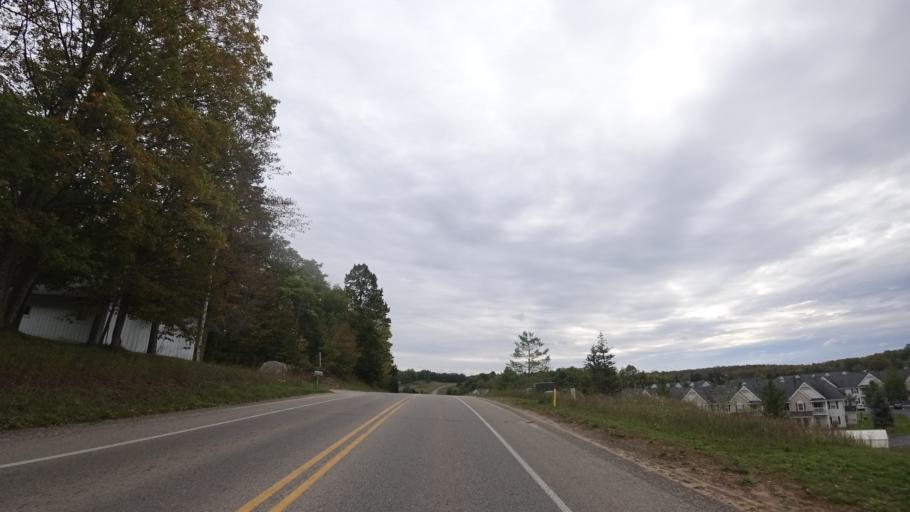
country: US
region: Michigan
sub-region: Emmet County
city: Petoskey
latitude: 45.3447
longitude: -84.9709
